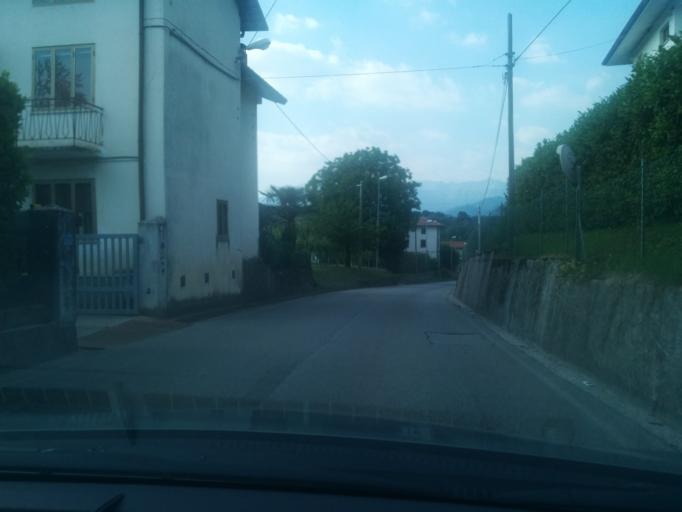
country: IT
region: Friuli Venezia Giulia
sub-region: Provincia di Udine
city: Tricesimo
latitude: 46.1779
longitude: 13.2434
